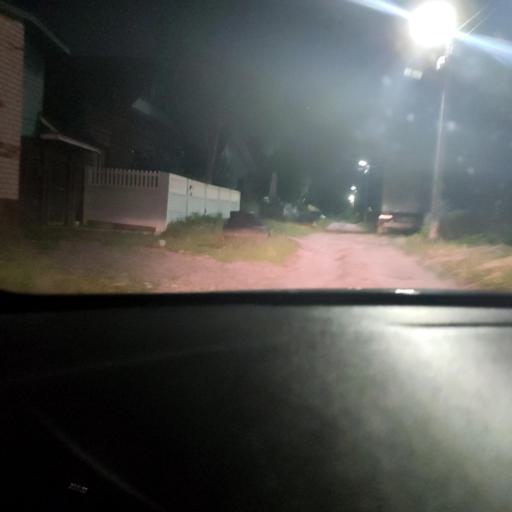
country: RU
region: Tatarstan
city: Staroye Arakchino
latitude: 55.8759
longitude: 49.0525
